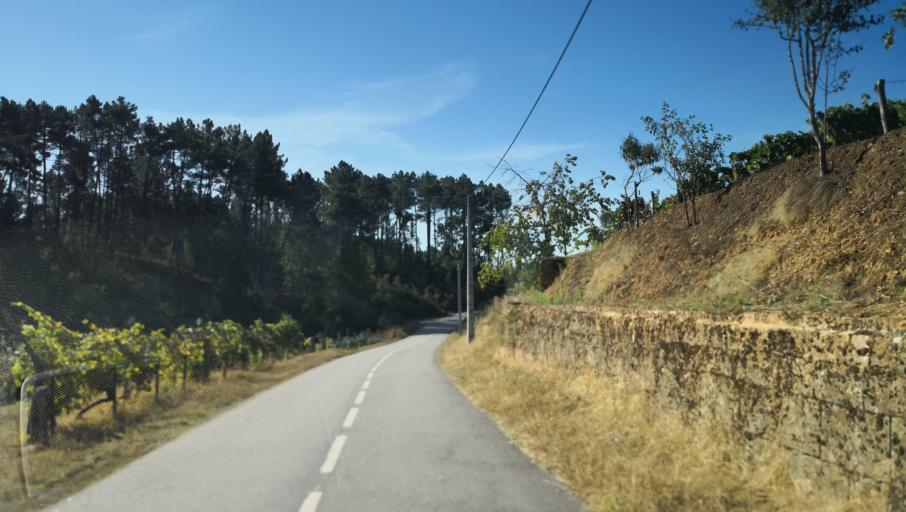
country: PT
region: Vila Real
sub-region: Sabrosa
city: Vilela
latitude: 41.2470
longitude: -7.6349
